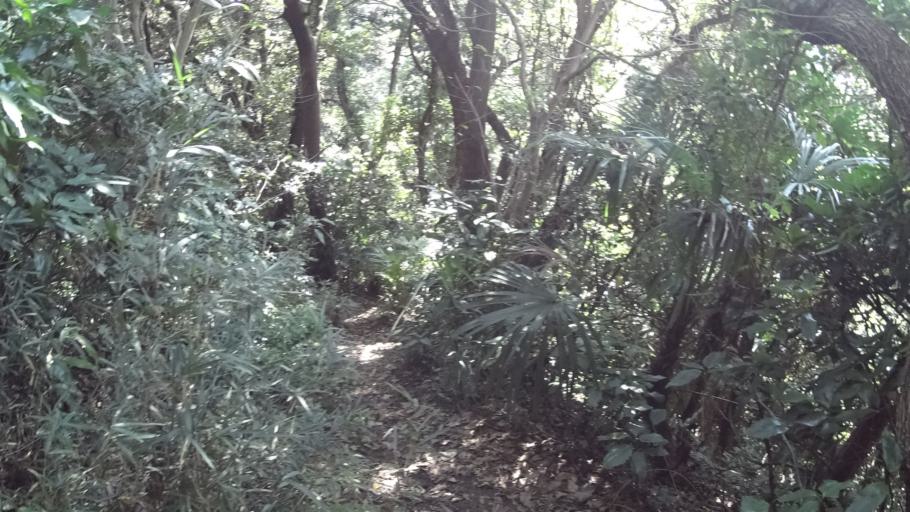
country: JP
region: Kanagawa
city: Hayama
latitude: 35.2753
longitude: 139.6039
